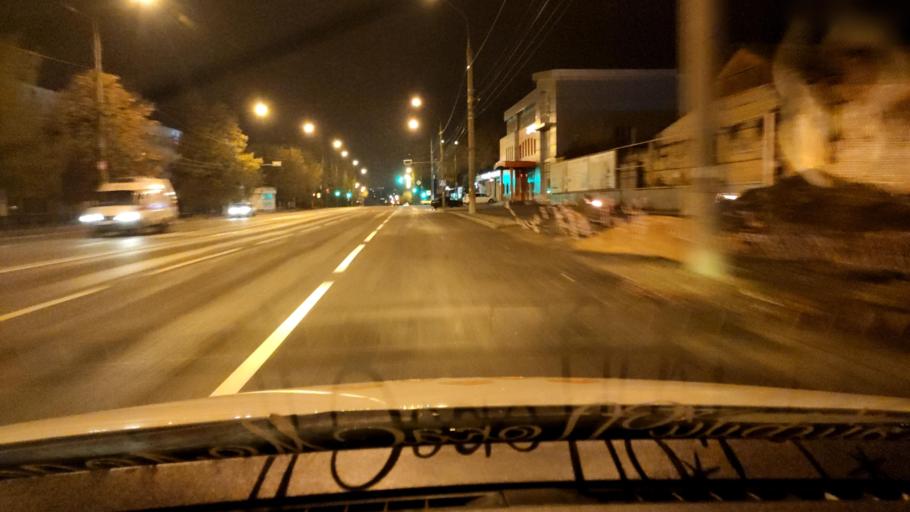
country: RU
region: Voronezj
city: Voronezh
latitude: 51.6861
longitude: 39.1655
